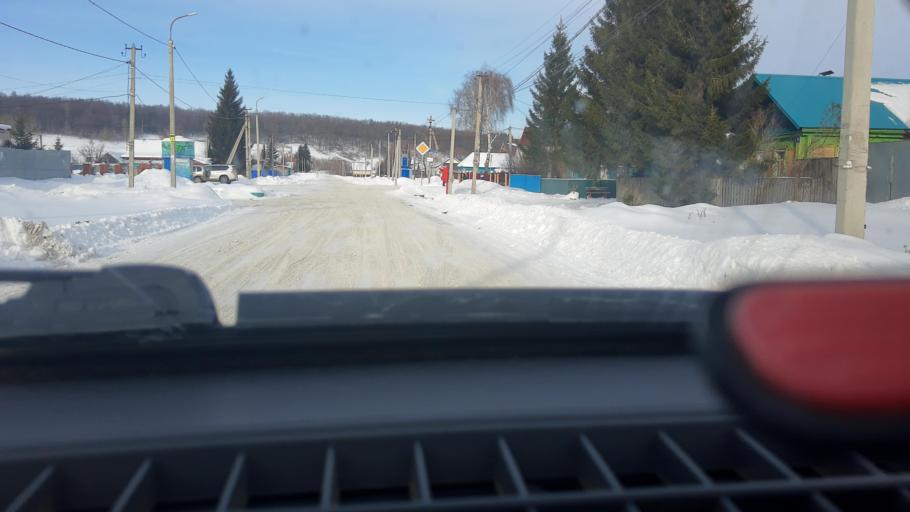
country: RU
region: Bashkortostan
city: Ufa
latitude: 54.5196
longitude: 55.9121
